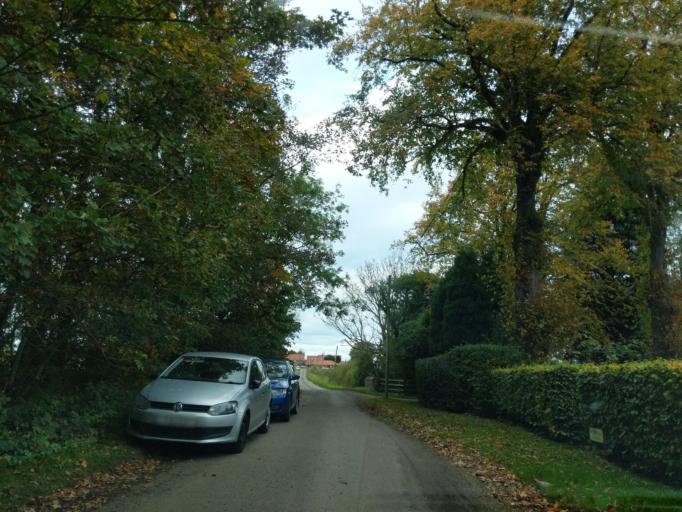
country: GB
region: Scotland
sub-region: East Lothian
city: Macmerry
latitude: 55.9466
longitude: -2.8665
